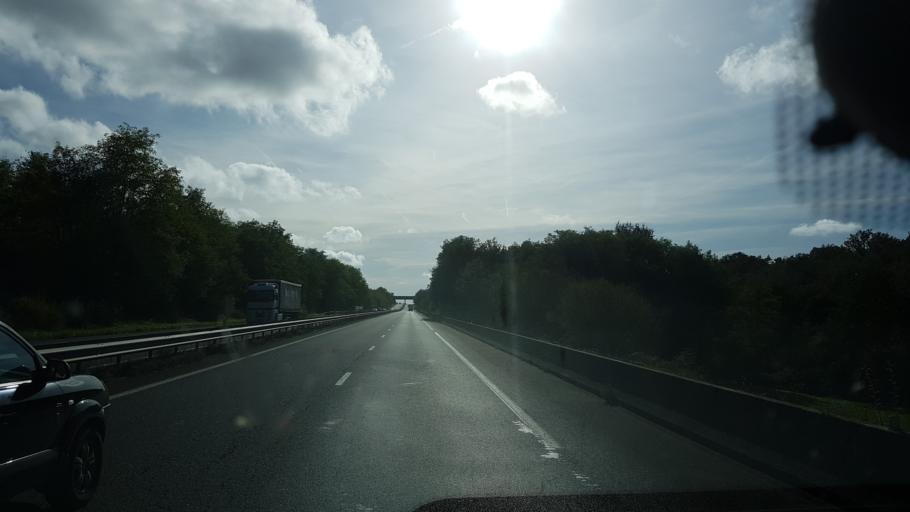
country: FR
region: Poitou-Charentes
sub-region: Departement de la Charente
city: Taponnat-Fleurignac
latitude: 45.7769
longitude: 0.4045
